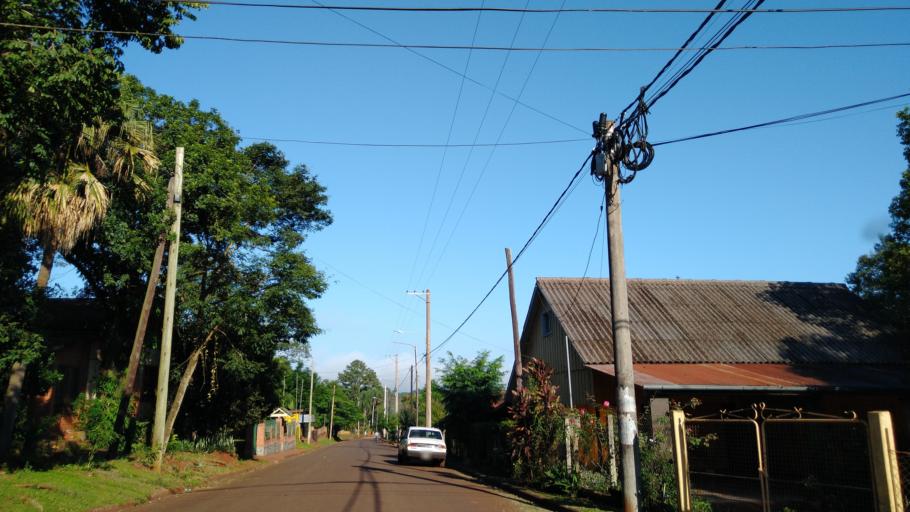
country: AR
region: Misiones
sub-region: Departamento de Montecarlo
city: Montecarlo
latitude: -26.5648
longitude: -54.7689
